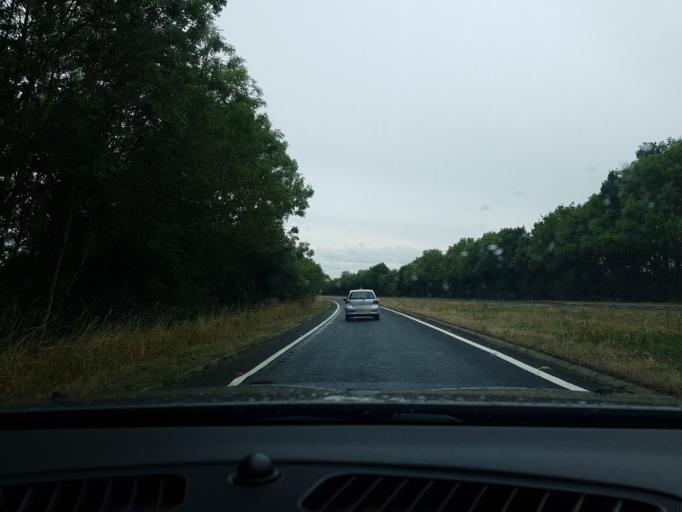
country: GB
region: England
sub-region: Hampshire
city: Odiham
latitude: 51.2606
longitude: -0.9308
